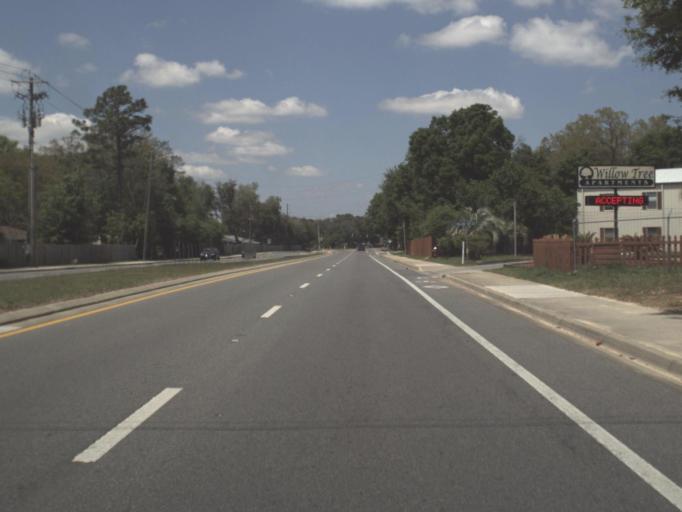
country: US
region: Florida
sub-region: Santa Rosa County
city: Point Baker
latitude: 30.6632
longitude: -87.0515
